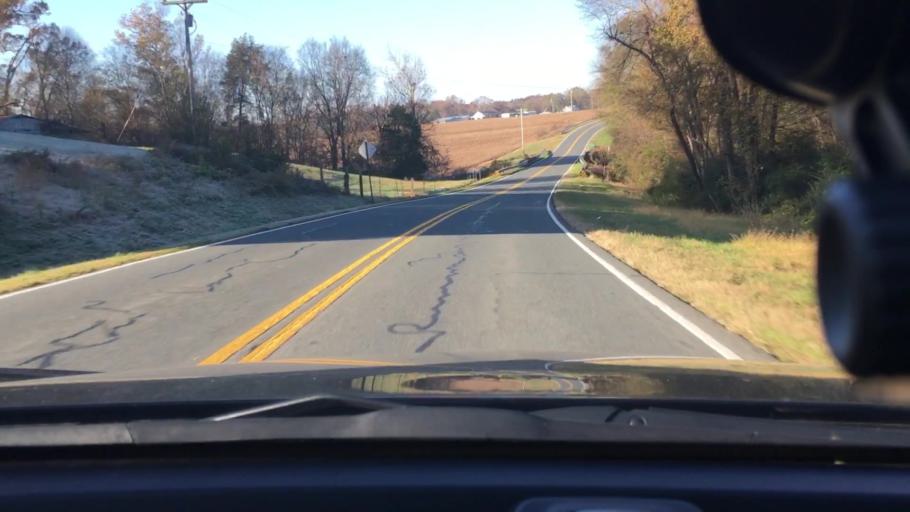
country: US
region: North Carolina
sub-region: Cabarrus County
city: Mount Pleasant
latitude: 35.3830
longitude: -80.3412
